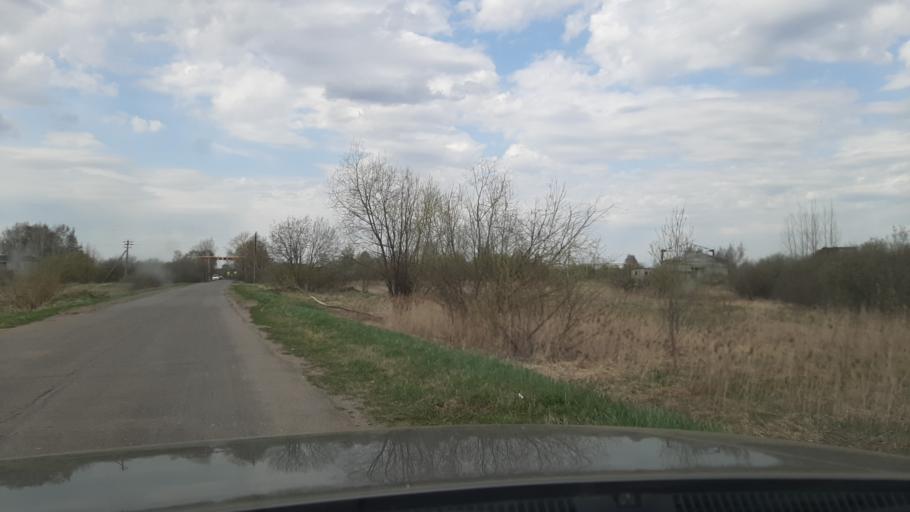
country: RU
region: Ivanovo
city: Privolzhsk
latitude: 57.3272
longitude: 41.2368
